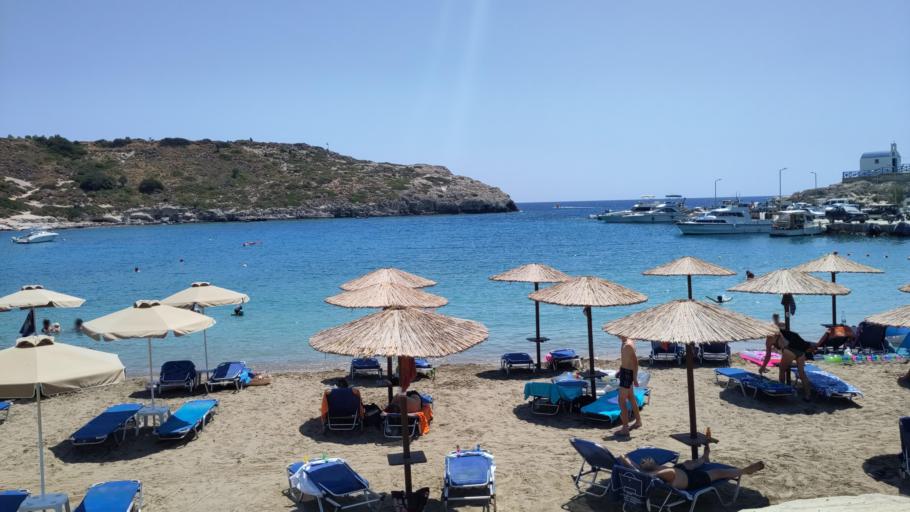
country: GR
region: South Aegean
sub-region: Nomos Dodekanisou
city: Afantou
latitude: 36.2499
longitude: 28.1690
